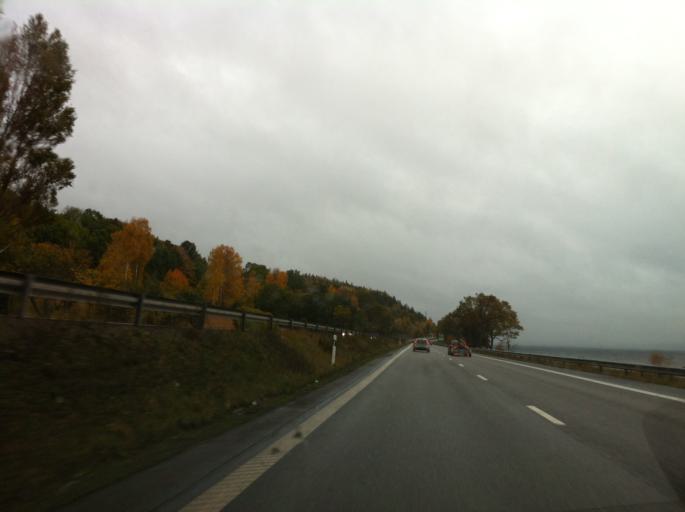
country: SE
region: Joenkoeping
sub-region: Jonkopings Kommun
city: Kaxholmen
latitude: 57.8784
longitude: 14.2773
